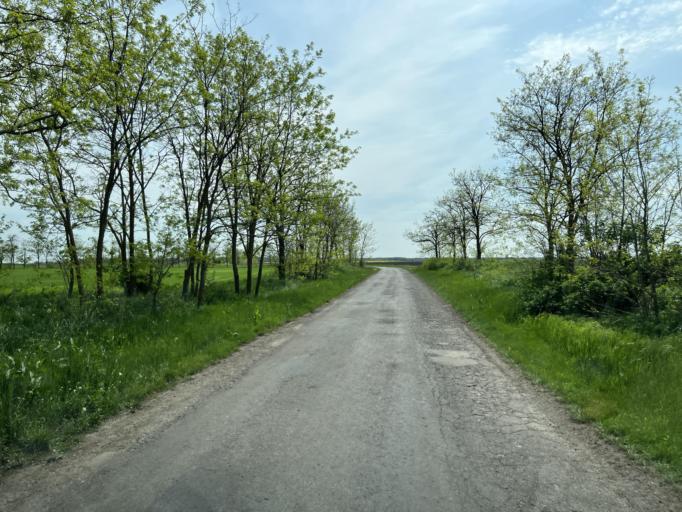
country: HU
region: Pest
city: Tapiogyorgye
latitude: 47.3007
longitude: 19.9802
